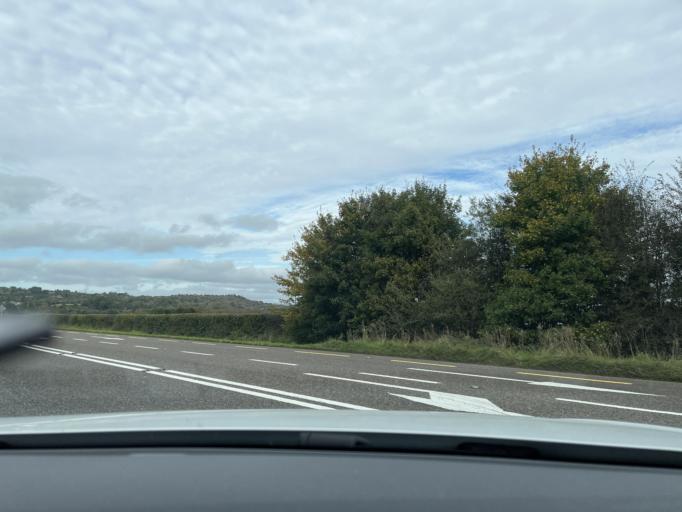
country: IE
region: Connaught
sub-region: Roscommon
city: Boyle
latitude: 53.9809
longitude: -8.2774
